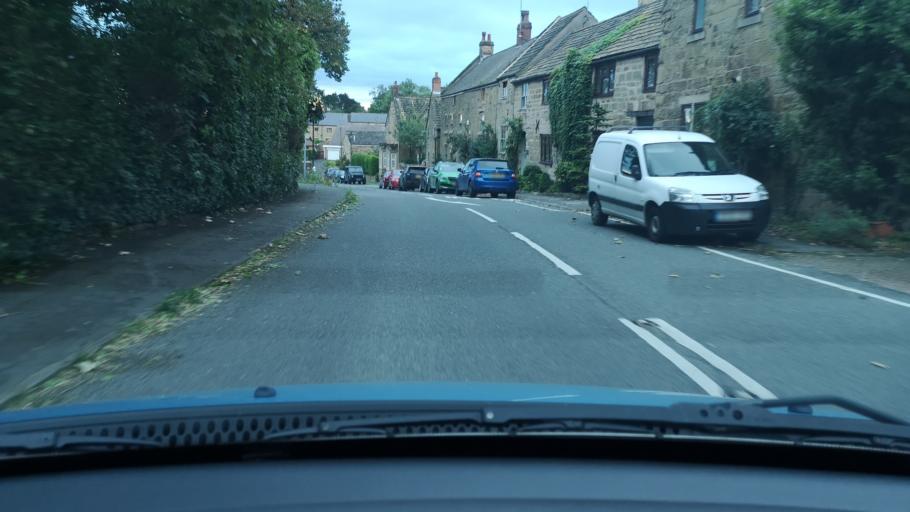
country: GB
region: England
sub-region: City and Borough of Wakefield
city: Badsworth
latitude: 53.6296
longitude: -1.3018
